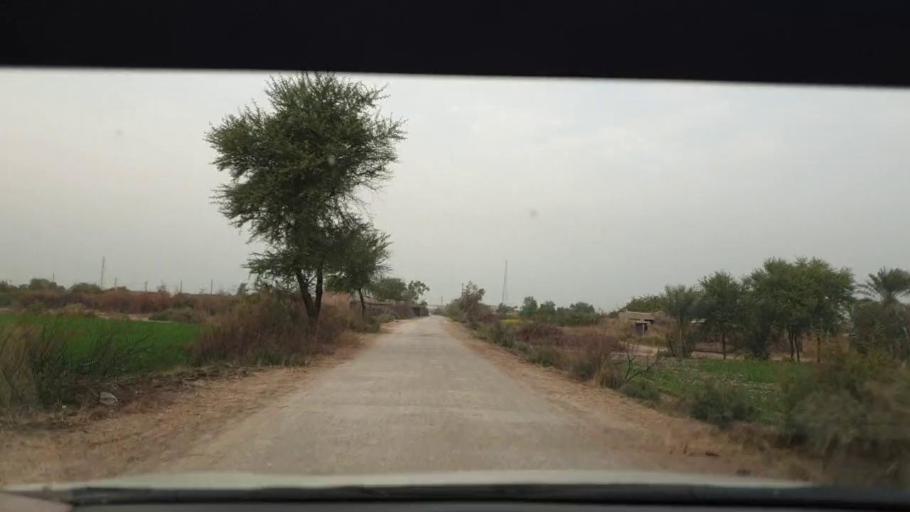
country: PK
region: Sindh
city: Sinjhoro
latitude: 25.9309
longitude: 68.7531
